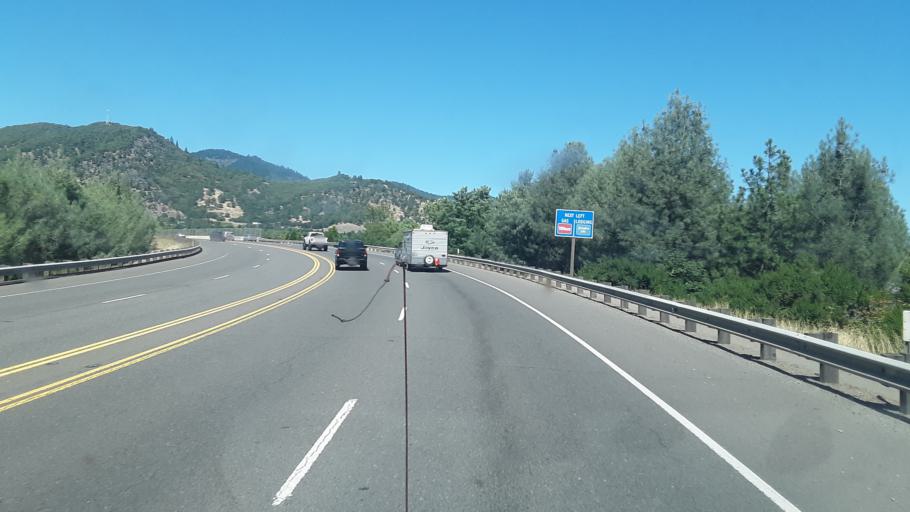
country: US
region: Oregon
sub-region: Josephine County
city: Fruitdale
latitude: 42.4330
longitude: -123.3137
